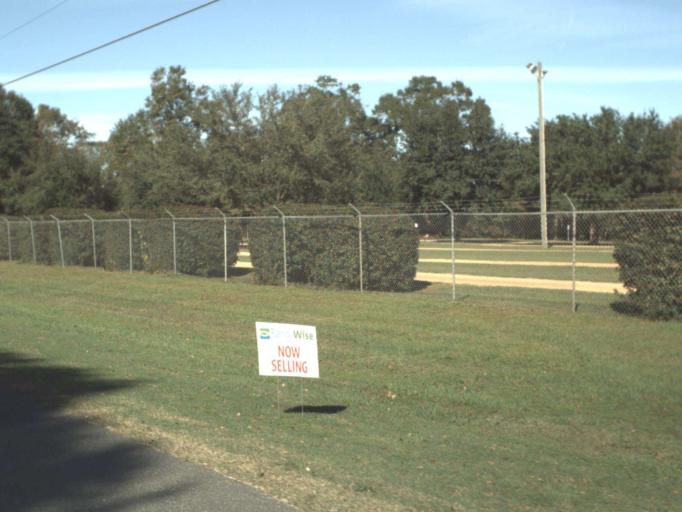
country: US
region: Florida
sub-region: Okaloosa County
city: Crestview
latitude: 30.7735
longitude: -86.6744
